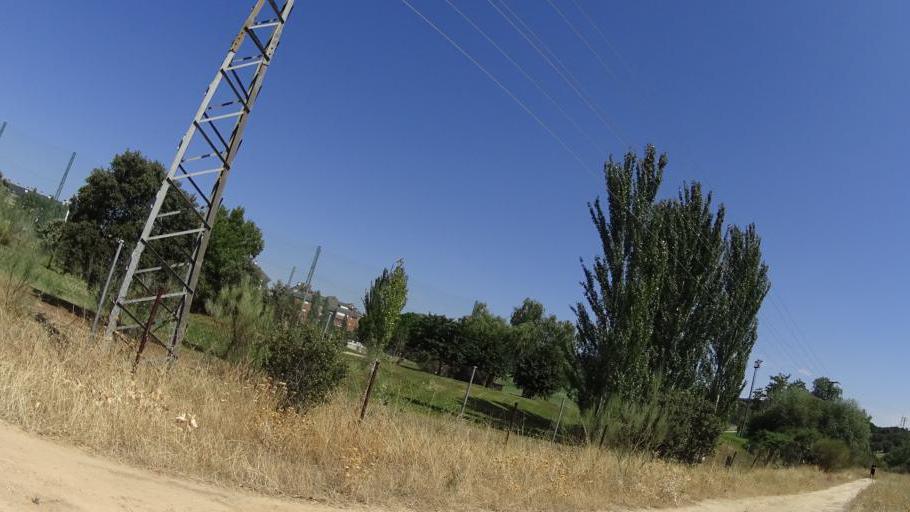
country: ES
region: Madrid
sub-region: Provincia de Madrid
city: Majadahonda
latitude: 40.4438
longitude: -3.8653
